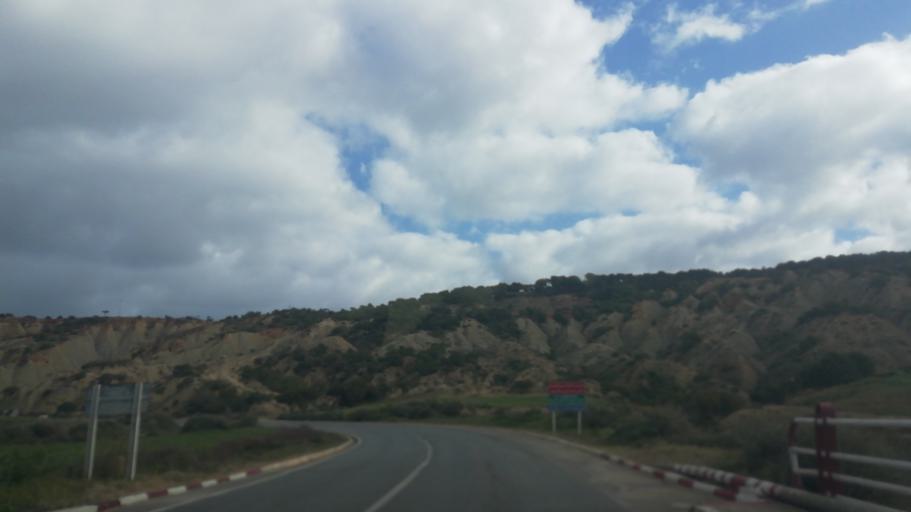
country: DZ
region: Relizane
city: Mazouna
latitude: 36.3040
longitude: 0.6706
